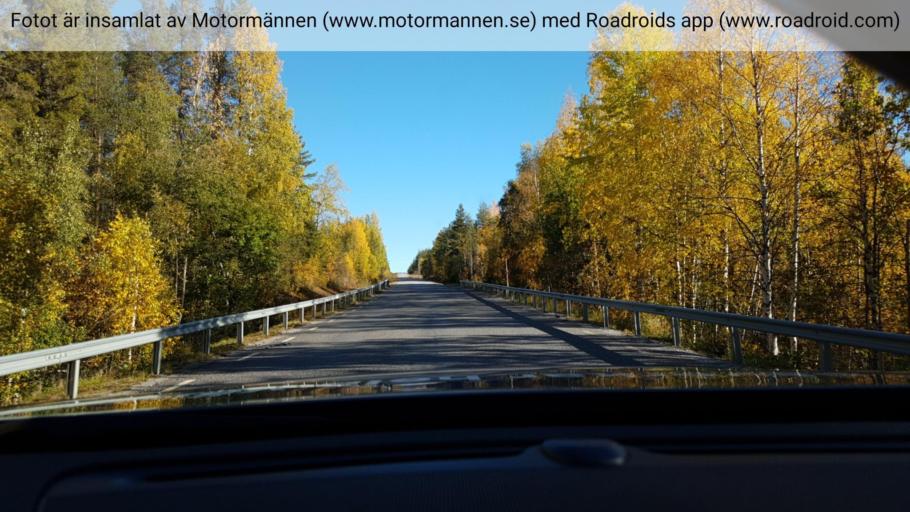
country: SE
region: Norrbotten
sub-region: Gallivare Kommun
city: Gaellivare
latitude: 66.4683
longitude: 20.8364
